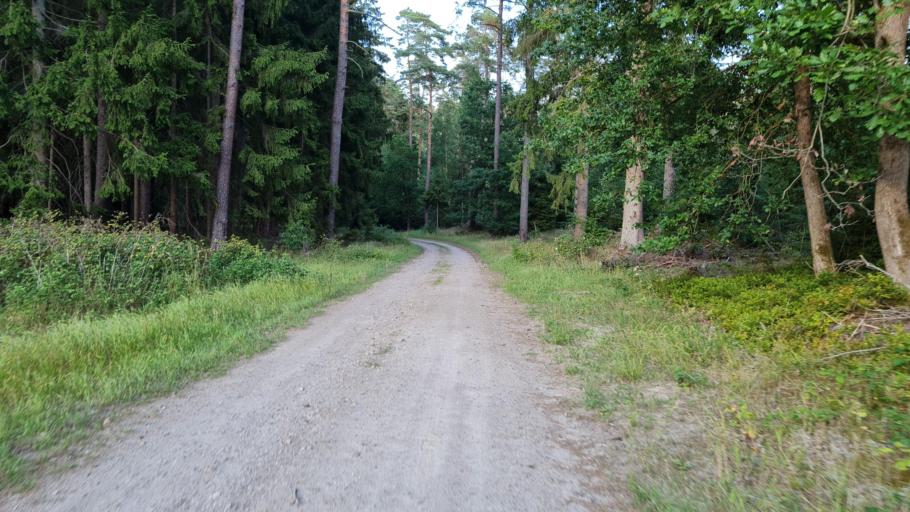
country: DE
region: Lower Saxony
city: Gohrde
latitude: 53.1660
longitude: 10.9095
